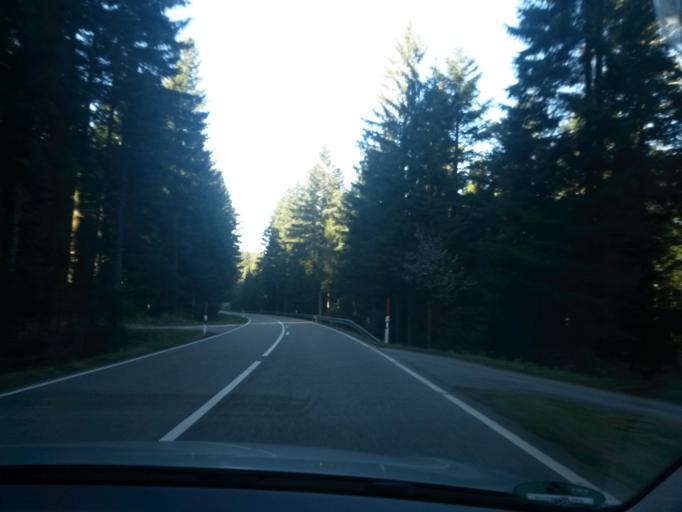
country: DE
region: Baden-Wuerttemberg
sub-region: Karlsruhe Region
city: Baiersbronn
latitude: 48.5484
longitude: 8.4278
